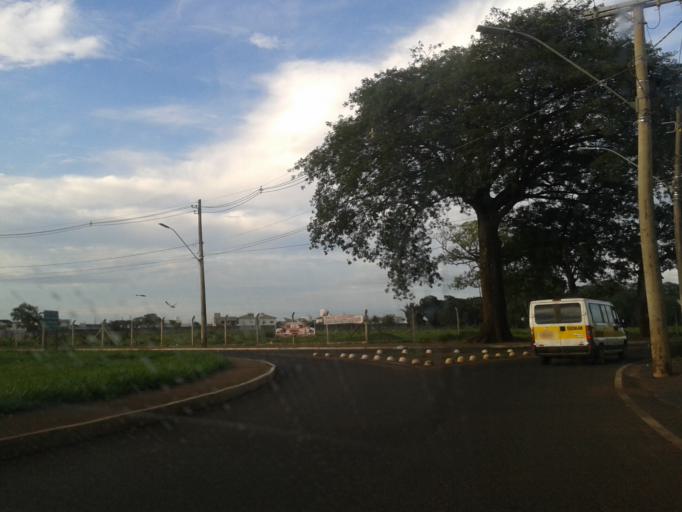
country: BR
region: Minas Gerais
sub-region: Araguari
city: Araguari
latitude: -18.6429
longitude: -48.2108
